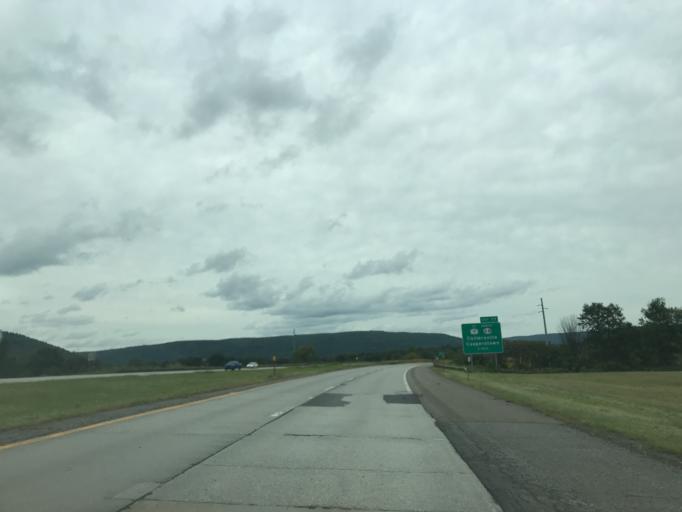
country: US
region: New York
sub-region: Otsego County
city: Oneonta
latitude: 42.4741
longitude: -74.9951
